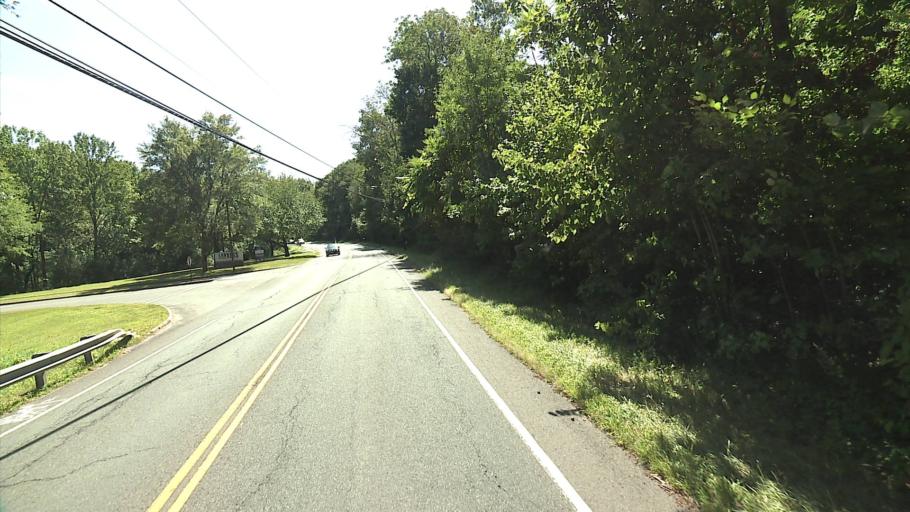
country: US
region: Connecticut
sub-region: New Haven County
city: Middlebury
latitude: 41.4880
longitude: -73.1598
